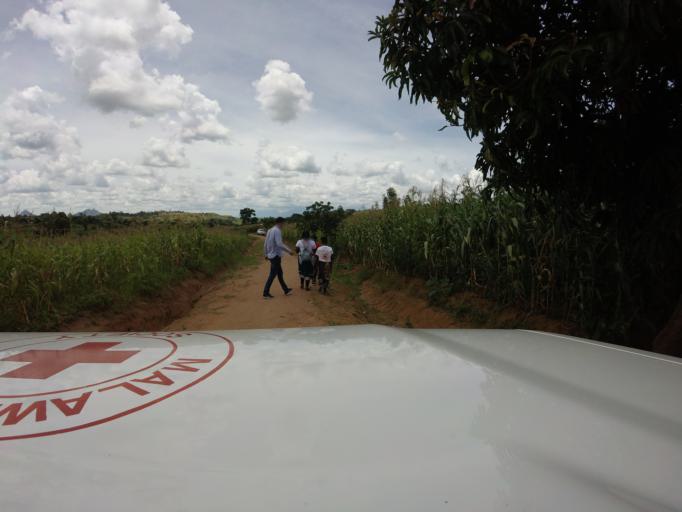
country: MW
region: Southern Region
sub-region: Thyolo District
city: Thyolo
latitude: -15.9599
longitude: 35.1629
